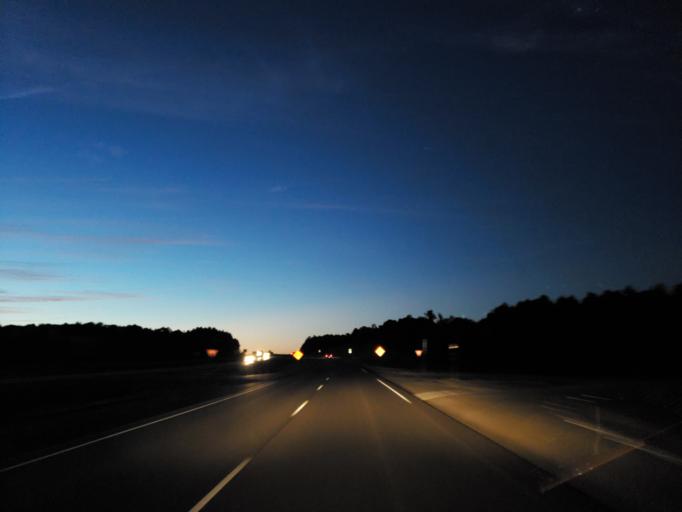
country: US
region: Mississippi
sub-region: Clarke County
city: Quitman
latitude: 32.1011
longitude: -88.7065
